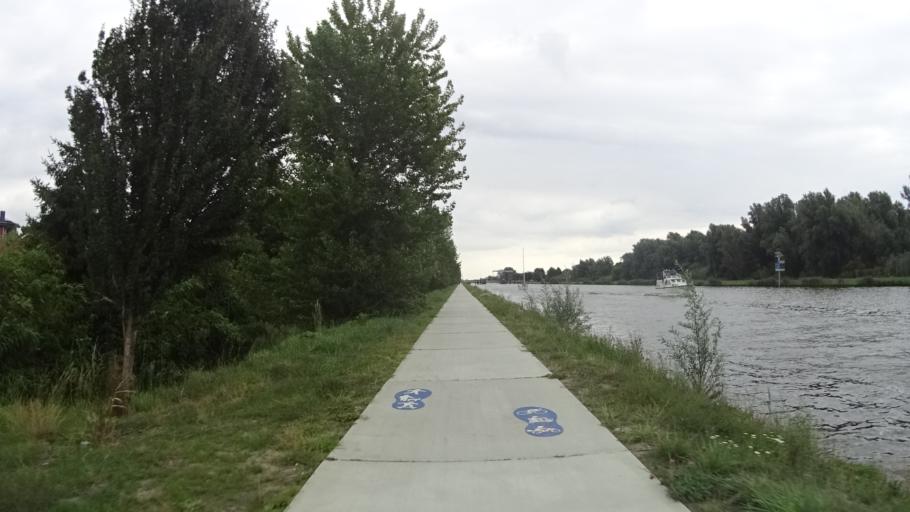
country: NL
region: Groningen
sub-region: Gemeente Groningen
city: Oosterpark
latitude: 53.2304
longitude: 6.6261
